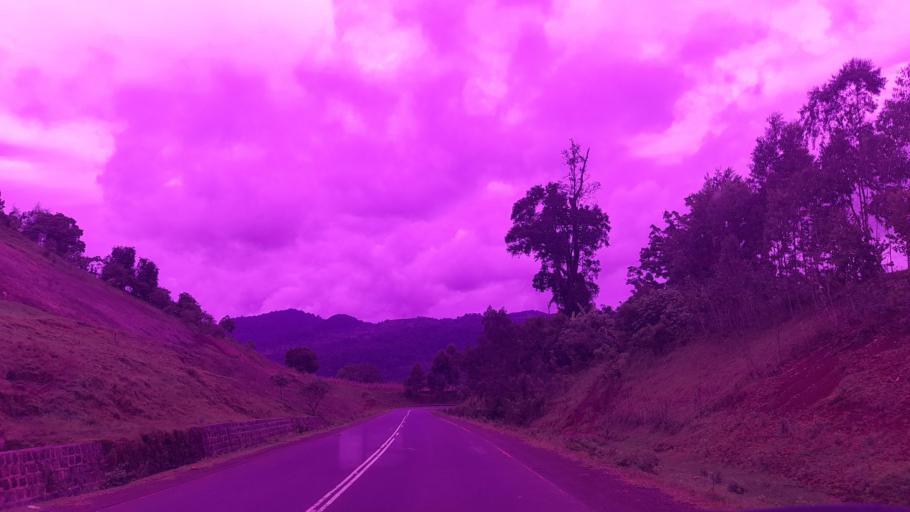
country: ET
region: Southern Nations, Nationalities, and People's Region
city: Bonga
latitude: 7.2862
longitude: 35.9747
